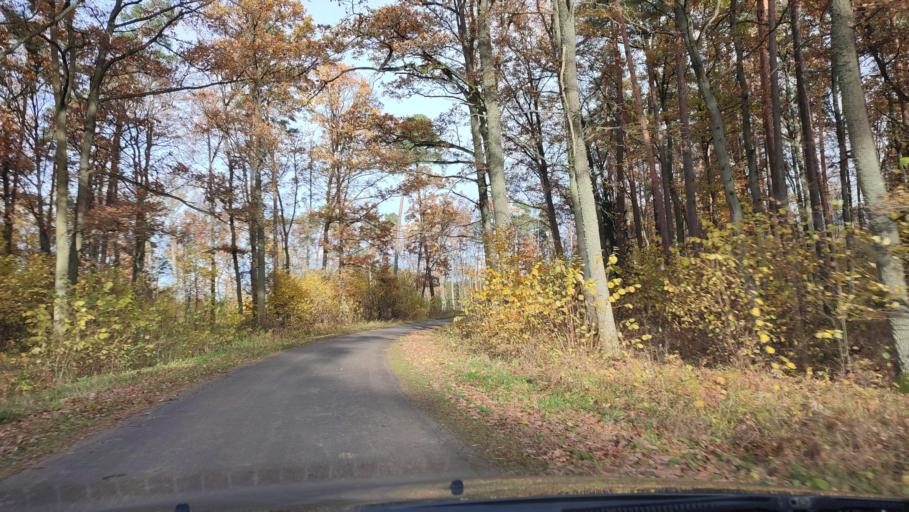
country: PL
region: Warmian-Masurian Voivodeship
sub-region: Powiat szczycienski
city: Szczytno
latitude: 53.5300
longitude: 20.9240
